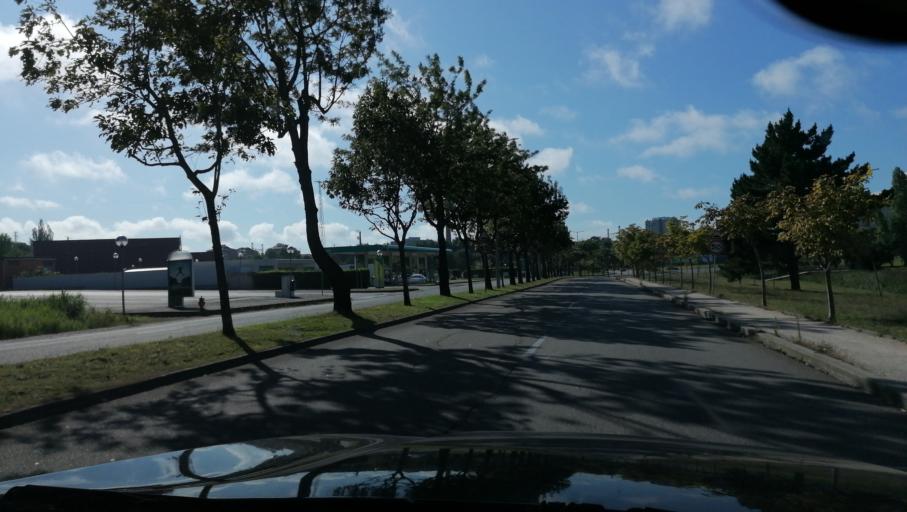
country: PT
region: Aveiro
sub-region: Aveiro
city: Aveiro
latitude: 40.6372
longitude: -8.6384
